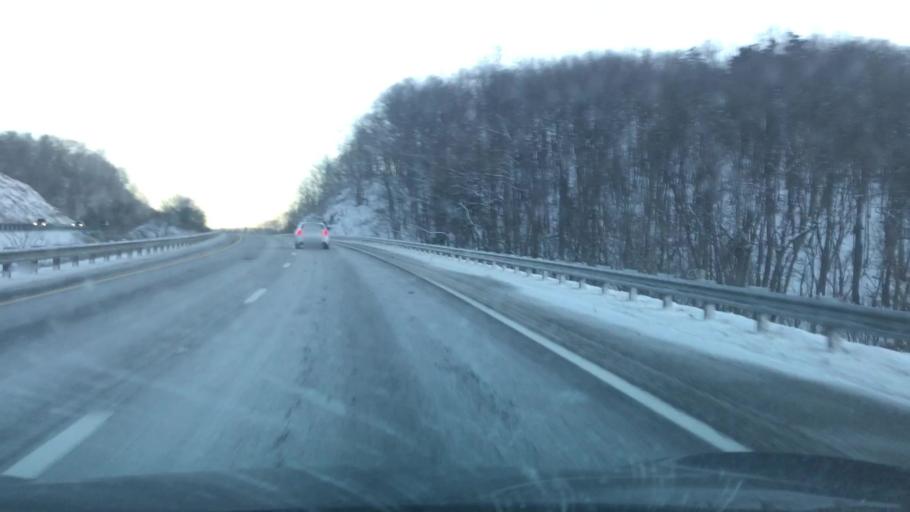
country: US
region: Virginia
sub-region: Montgomery County
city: Shawsville
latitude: 37.1971
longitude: -80.2685
